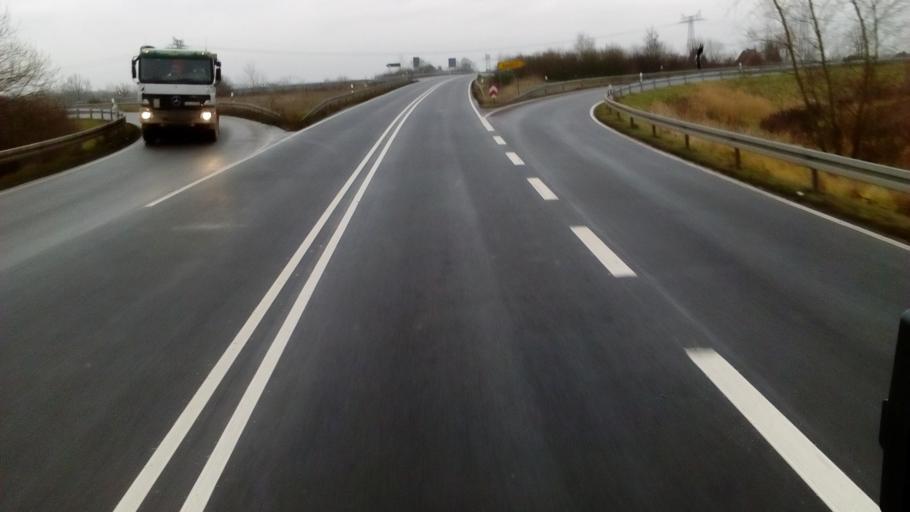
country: DE
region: Brandenburg
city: Perleberg
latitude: 53.0886
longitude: 11.8409
